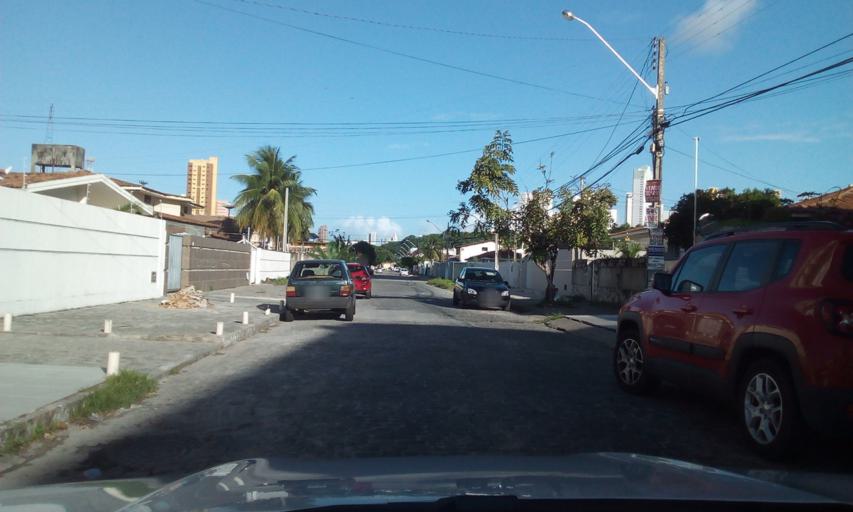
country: BR
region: Paraiba
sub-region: Joao Pessoa
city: Joao Pessoa
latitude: -7.1063
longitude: -34.8392
